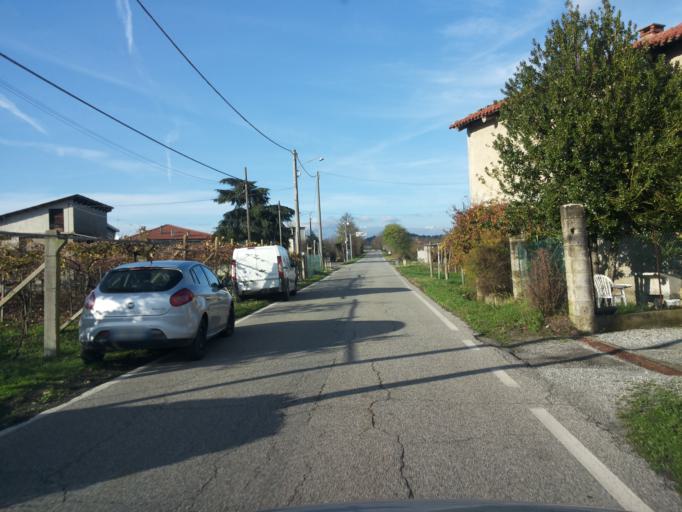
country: IT
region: Piedmont
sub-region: Provincia di Vercelli
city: Alice Castello
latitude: 45.3756
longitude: 8.0725
